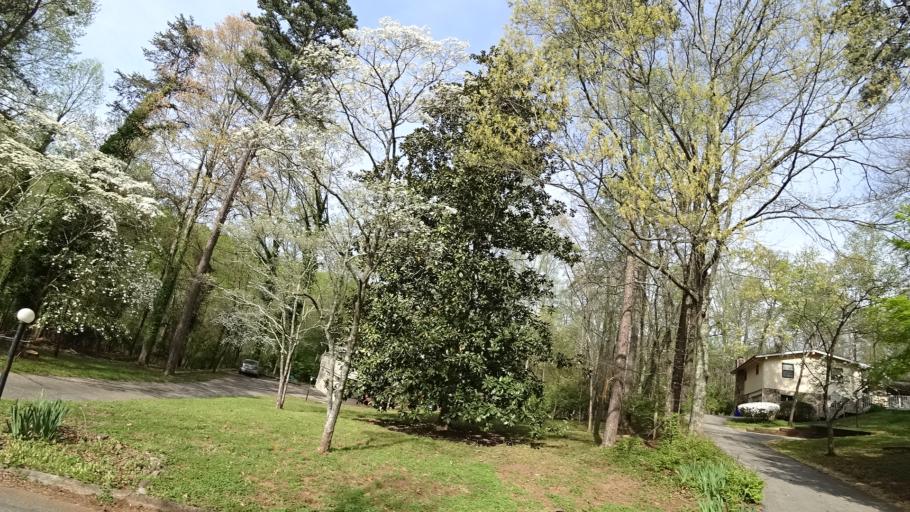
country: US
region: Tennessee
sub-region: Knox County
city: Knoxville
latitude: 35.9011
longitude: -83.9868
